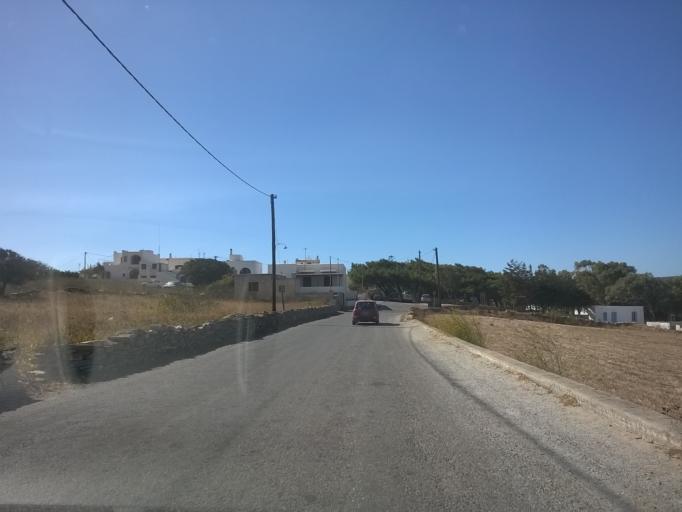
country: GR
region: South Aegean
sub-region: Nomos Kykladon
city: Filotion
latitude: 37.0418
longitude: 25.4378
